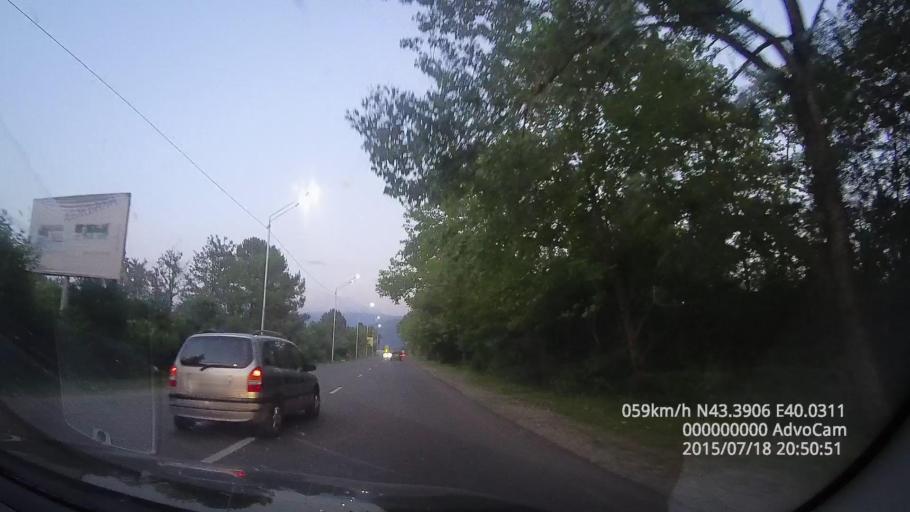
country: GE
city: Gantiadi
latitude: 43.3904
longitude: 40.0326
